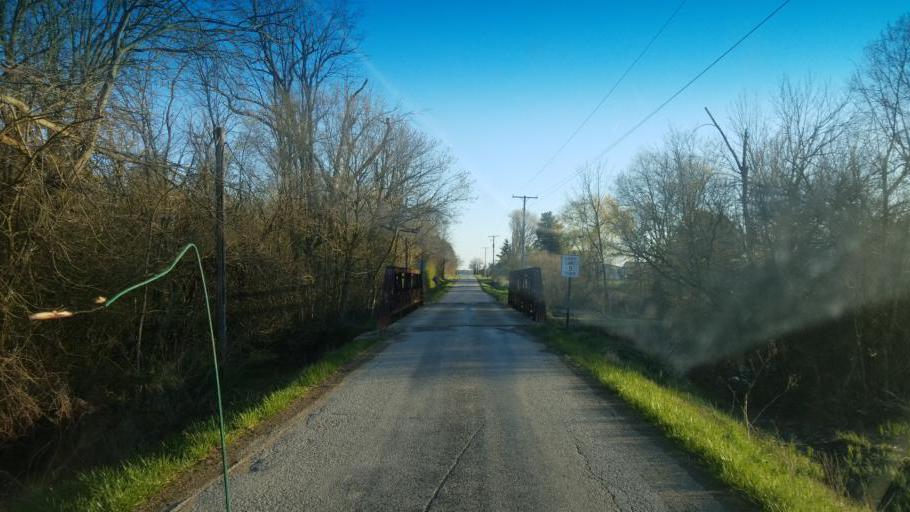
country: US
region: Ohio
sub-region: Morrow County
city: Cardington
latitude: 40.5441
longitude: -82.9194
